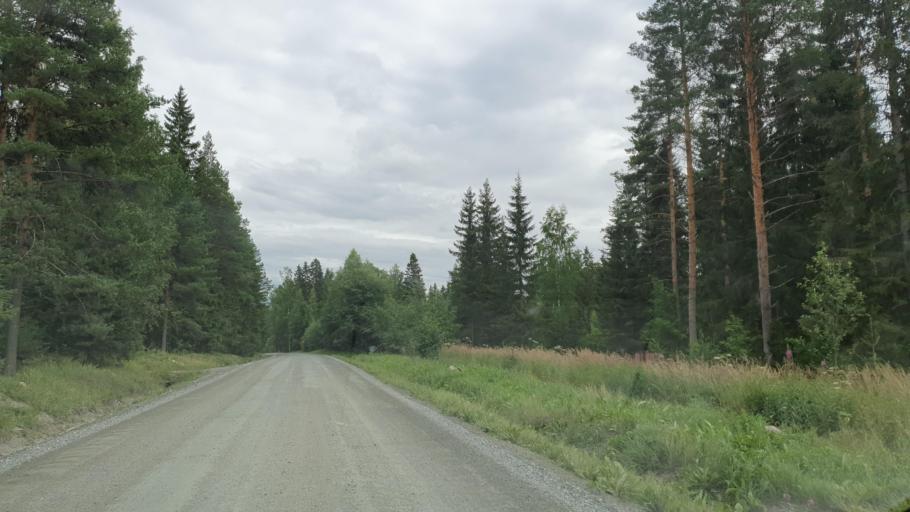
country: FI
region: Northern Savo
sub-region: Ylae-Savo
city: Iisalmi
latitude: 63.5163
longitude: 27.1094
